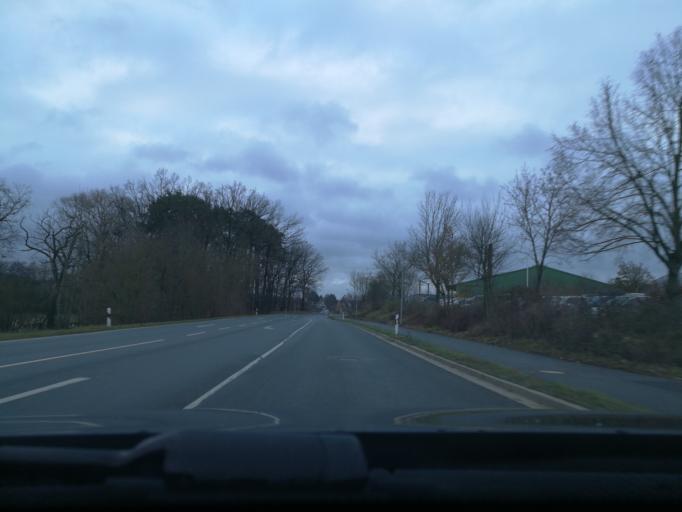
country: DE
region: Bavaria
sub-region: Regierungsbezirk Mittelfranken
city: Heroldsberg
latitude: 49.5449
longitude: 11.1507
